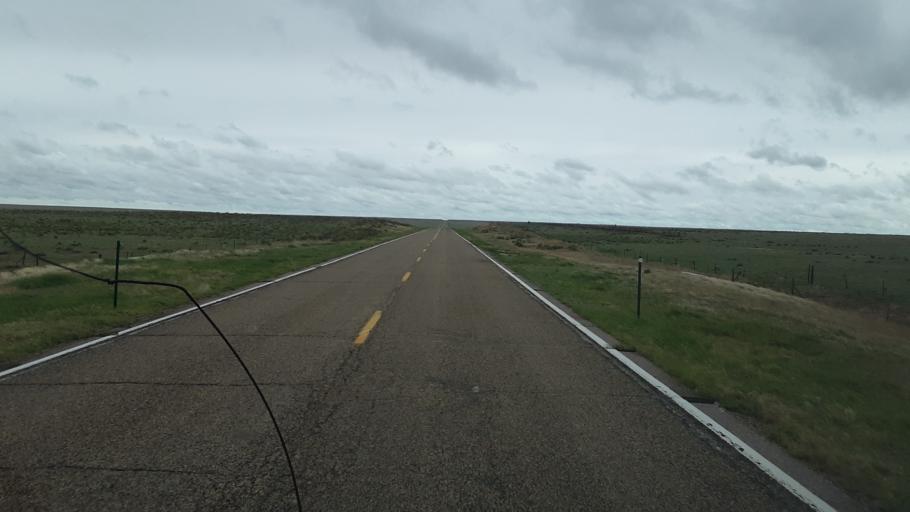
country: US
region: Colorado
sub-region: Lincoln County
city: Hugo
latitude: 38.8499
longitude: -103.3514
